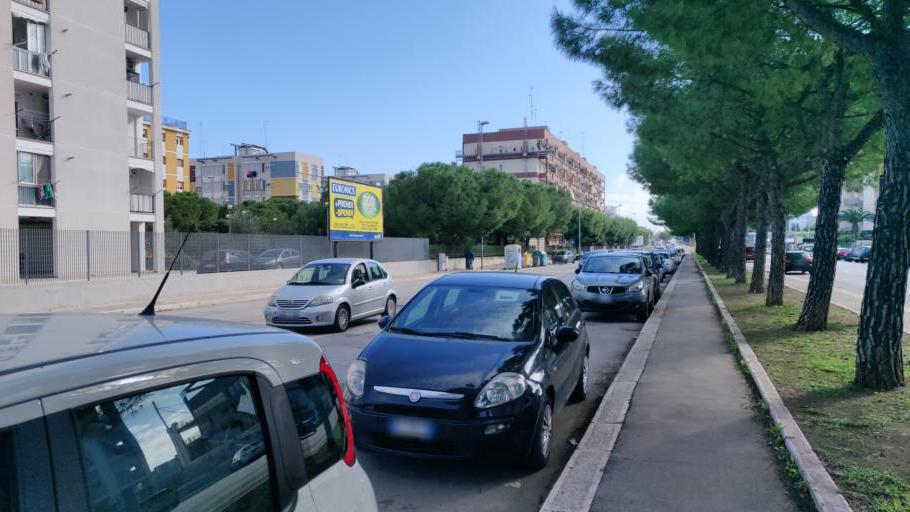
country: IT
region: Apulia
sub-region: Provincia di Bari
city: Bari
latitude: 41.1074
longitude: 16.8968
